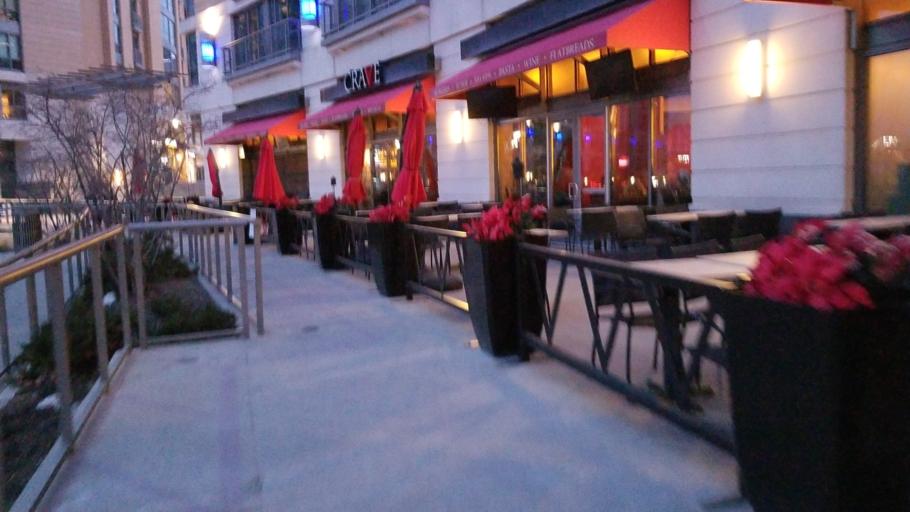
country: US
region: Nebraska
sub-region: Douglas County
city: Omaha
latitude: 41.2587
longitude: -95.9604
